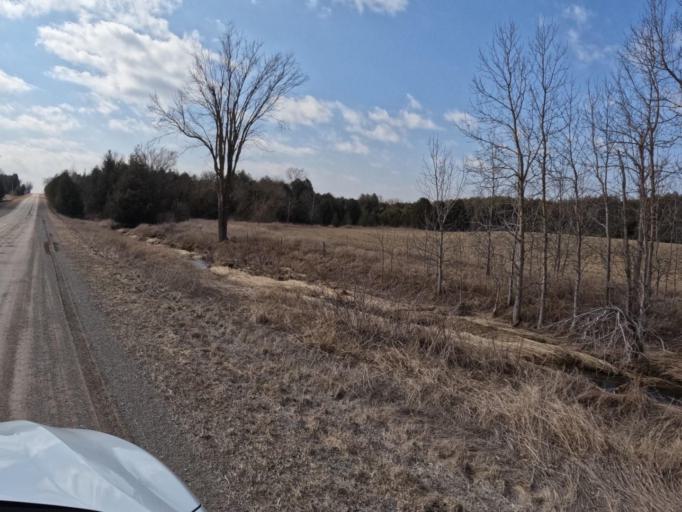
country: CA
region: Ontario
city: Orangeville
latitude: 43.9199
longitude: -80.2553
